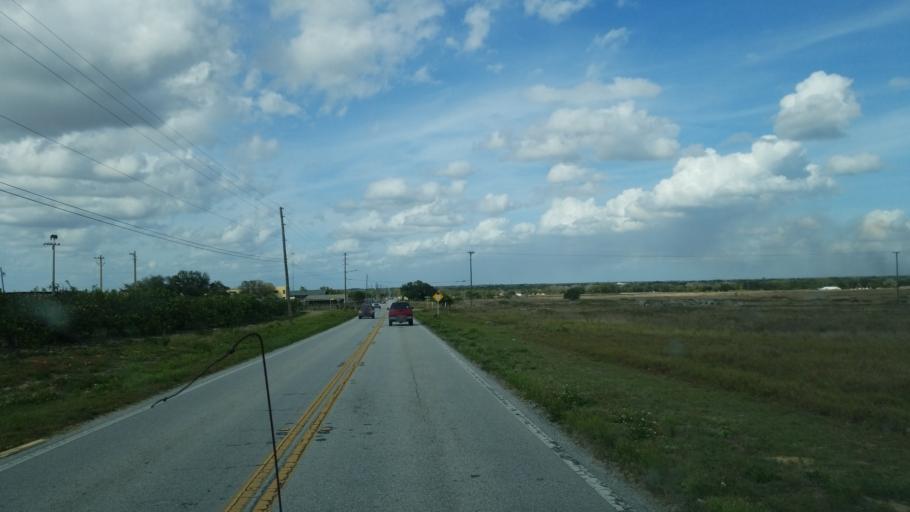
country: US
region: Florida
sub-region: Polk County
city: Haines City
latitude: 28.0945
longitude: -81.6068
